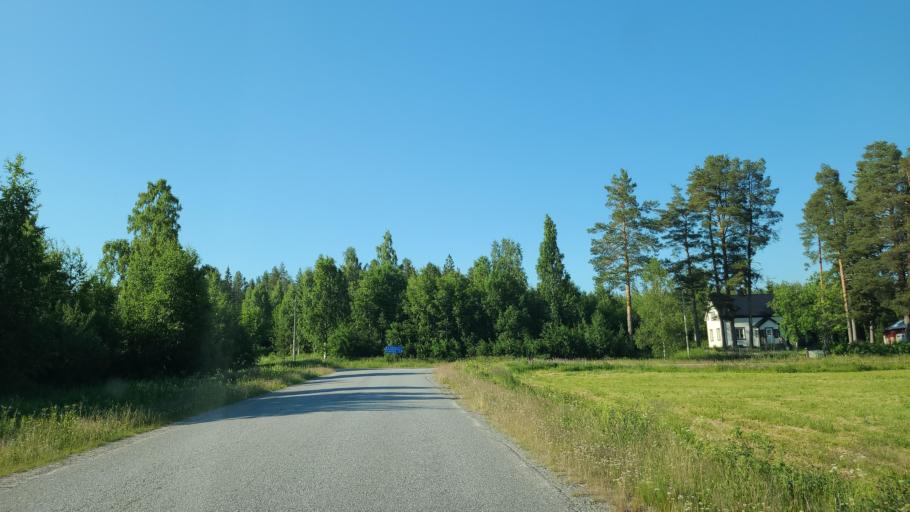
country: SE
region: Vaesterbotten
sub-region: Robertsfors Kommun
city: Robertsfors
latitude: 64.3092
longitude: 20.7796
